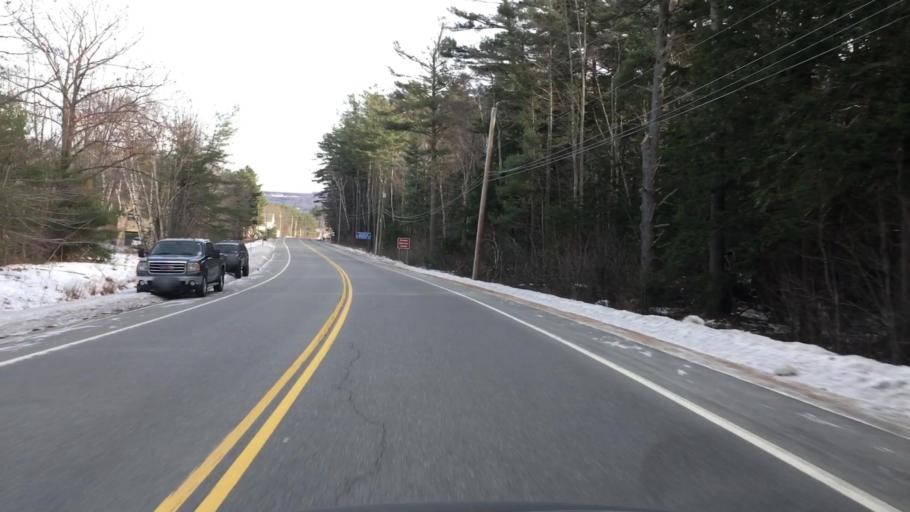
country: US
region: New Hampshire
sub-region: Sullivan County
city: Sunapee
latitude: 43.3414
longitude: -72.0794
